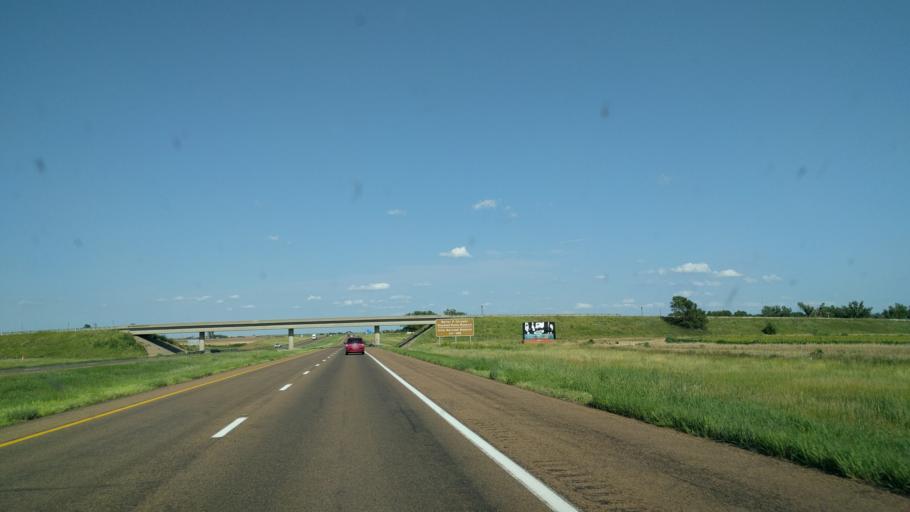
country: US
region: Kansas
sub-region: Ellis County
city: Ellis
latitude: 38.9501
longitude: -99.5787
